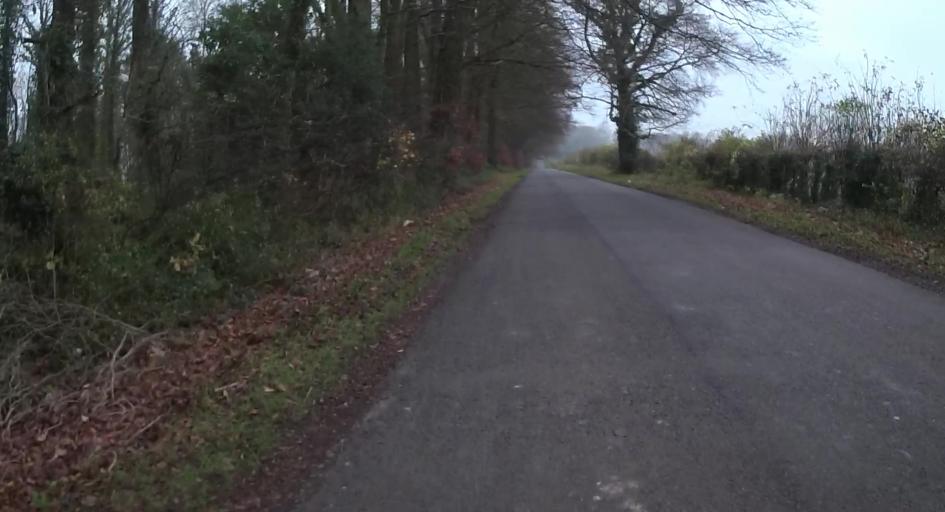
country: GB
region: England
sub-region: Hampshire
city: Kings Worthy
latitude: 51.1220
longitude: -1.2113
